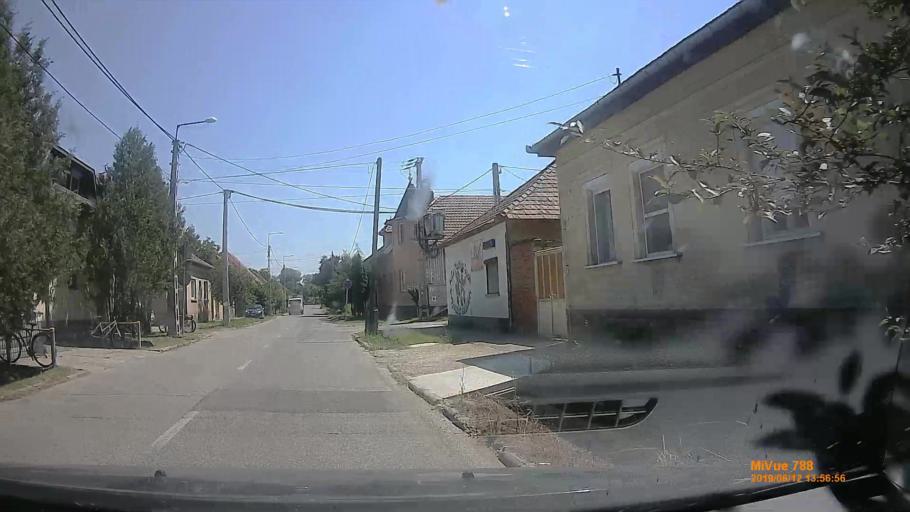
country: HU
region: Csongrad
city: Szeged
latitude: 46.2613
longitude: 20.1810
